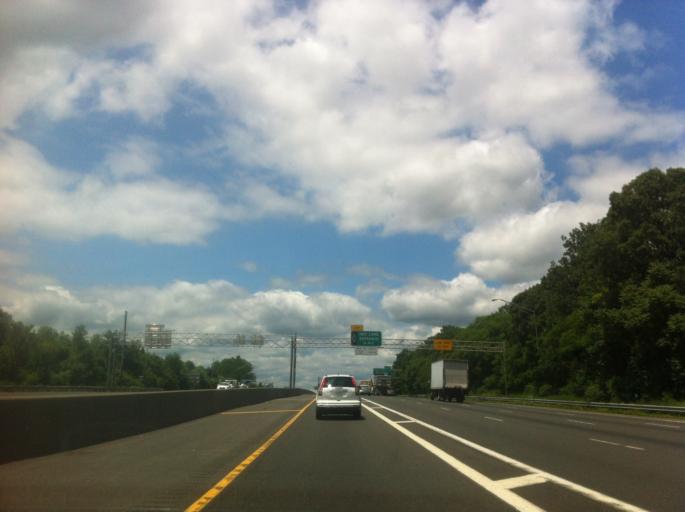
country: US
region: New York
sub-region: Suffolk County
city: Melville
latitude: 40.7828
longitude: -73.4347
